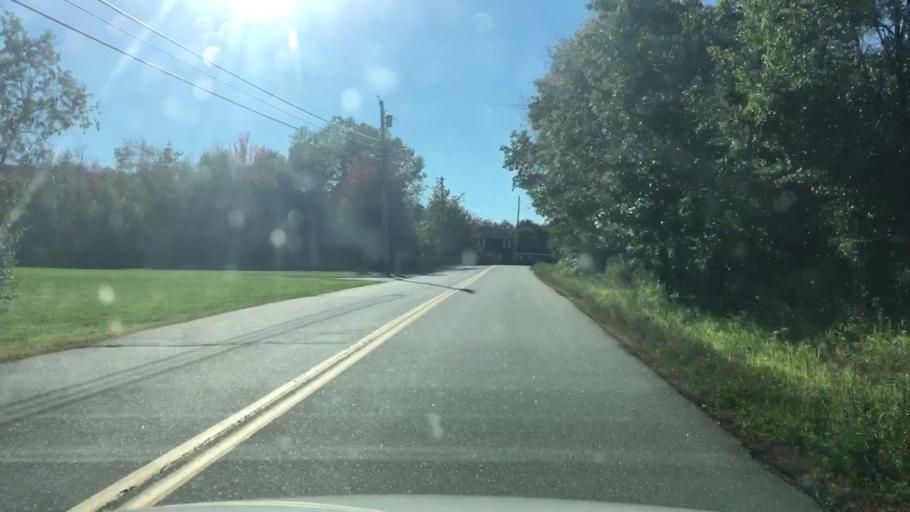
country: US
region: Maine
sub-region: Androscoggin County
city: Lewiston
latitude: 44.0778
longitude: -70.1594
